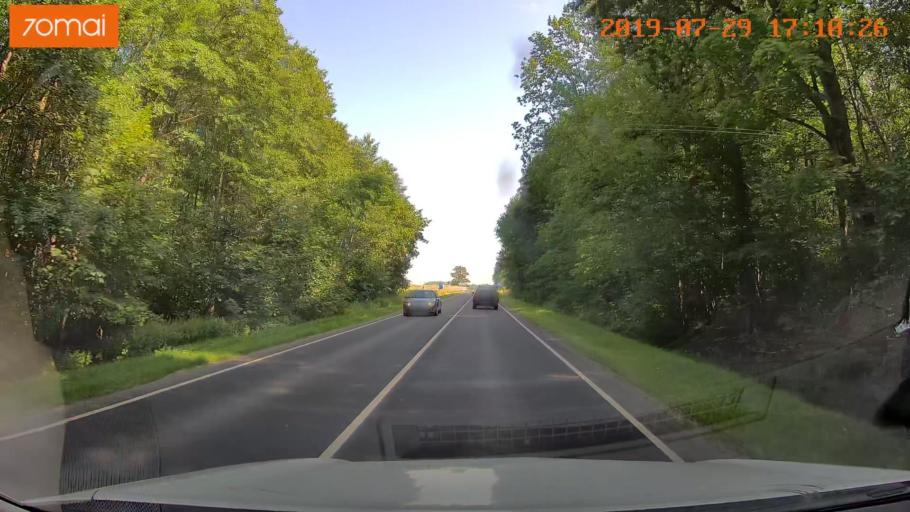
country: RU
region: Kaliningrad
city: Vzmorye
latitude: 54.8022
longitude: 20.3687
